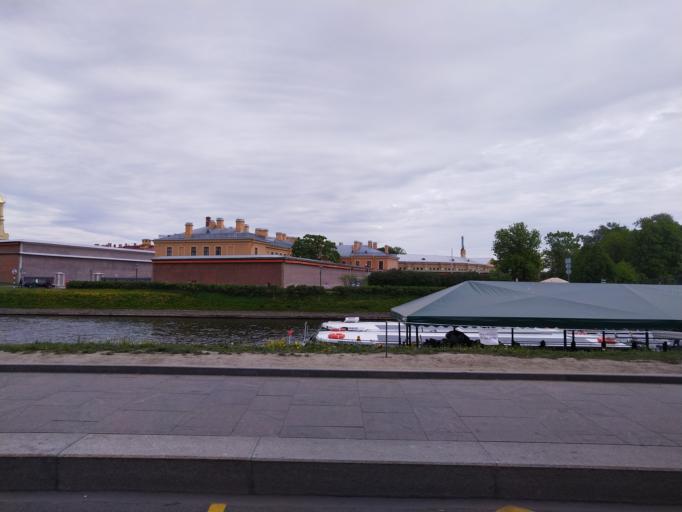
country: RU
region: St.-Petersburg
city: Saint Petersburg
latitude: 59.9502
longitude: 30.3090
